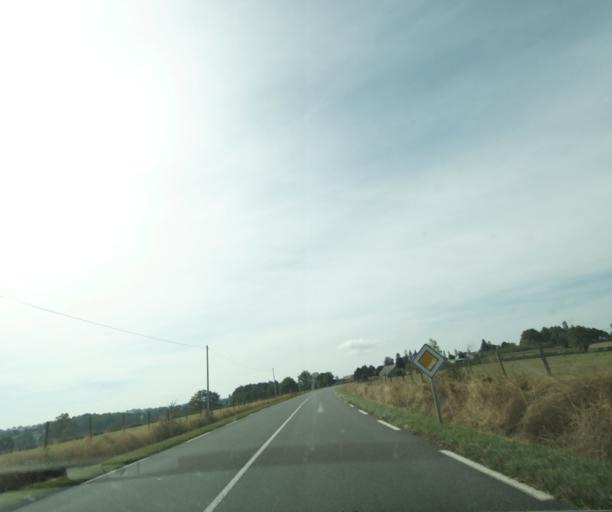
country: FR
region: Auvergne
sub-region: Departement de l'Allier
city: Le Donjon
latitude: 46.3340
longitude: 3.7728
